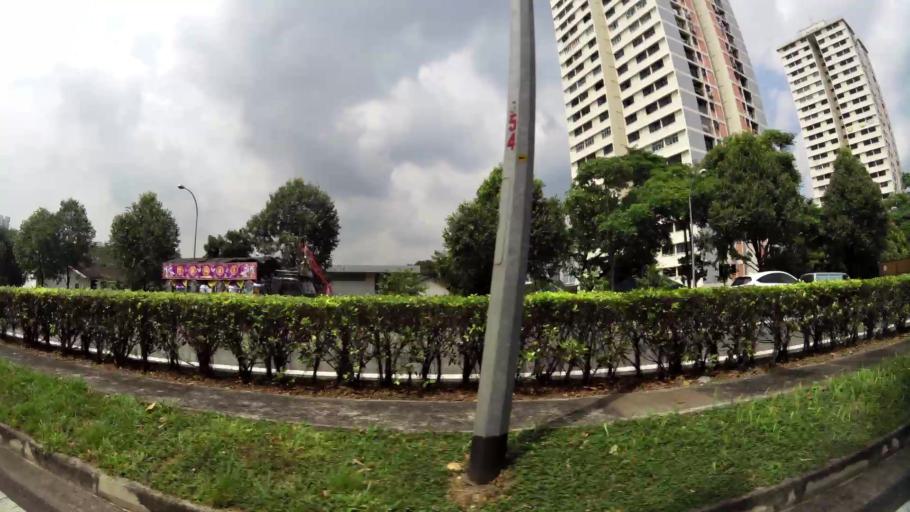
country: SG
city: Singapore
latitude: 1.3177
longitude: 103.8747
